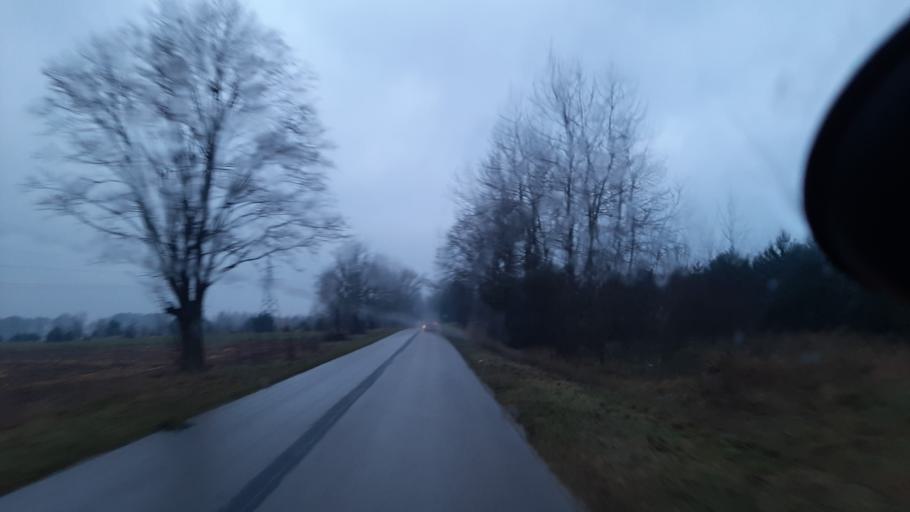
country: PL
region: Lublin Voivodeship
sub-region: Powiat lubartowski
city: Firlej
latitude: 51.5568
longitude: 22.5356
